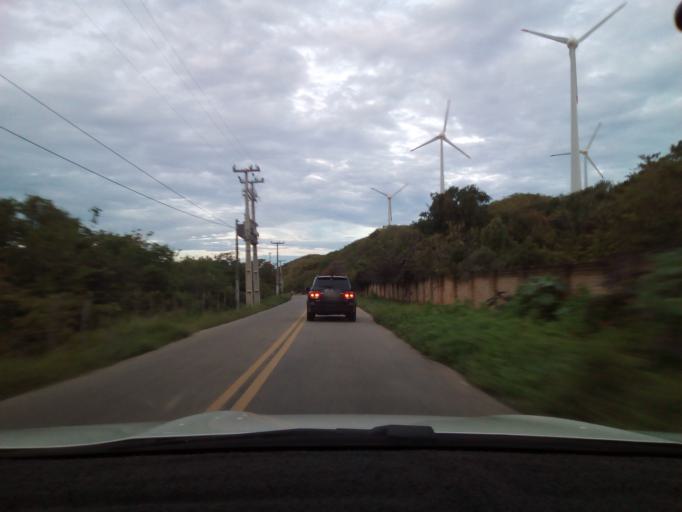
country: BR
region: Ceara
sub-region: Beberibe
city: Beberibe
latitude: -4.1837
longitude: -38.0911
